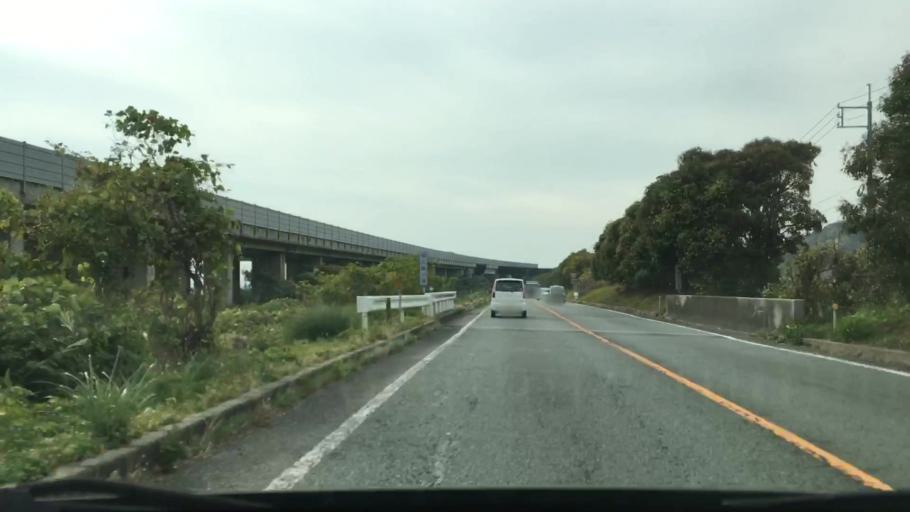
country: JP
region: Yamaguchi
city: Hofu
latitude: 34.0523
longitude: 131.5241
